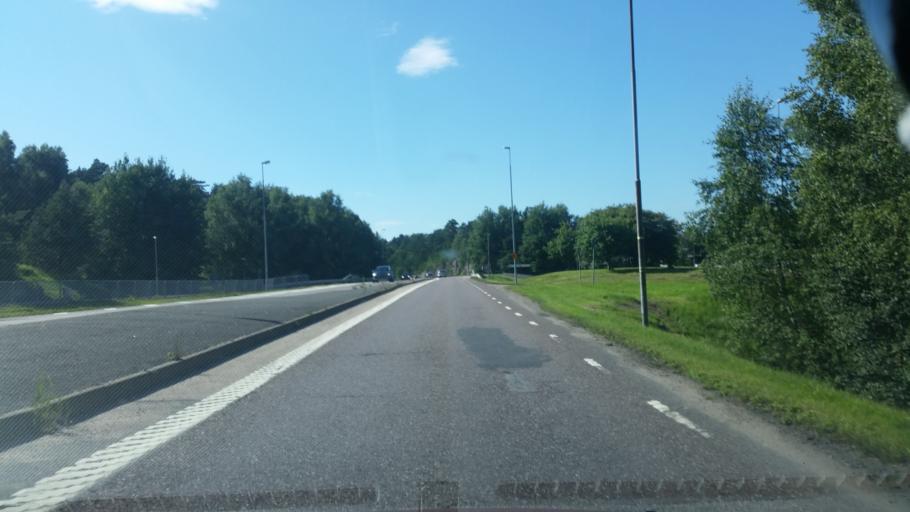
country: SE
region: Vaestra Goetaland
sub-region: Partille Kommun
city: Furulund
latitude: 57.7240
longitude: 12.1289
